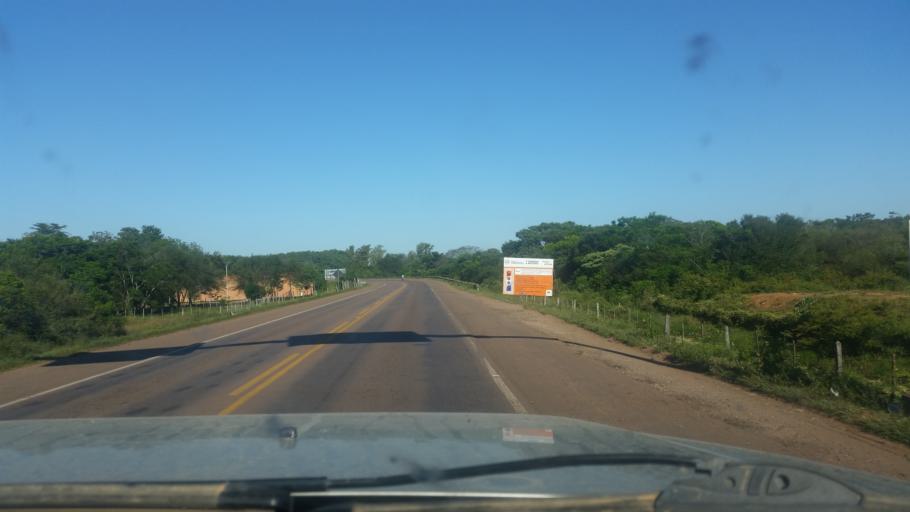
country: PY
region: Paraguari
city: Paraguari
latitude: -25.6328
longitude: -57.1469
